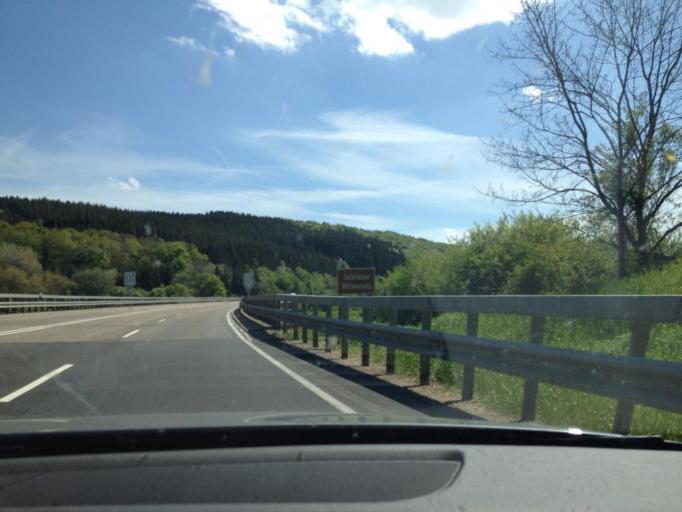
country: DE
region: Rheinland-Pfalz
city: Weinsheim
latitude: 50.2489
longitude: 6.4687
